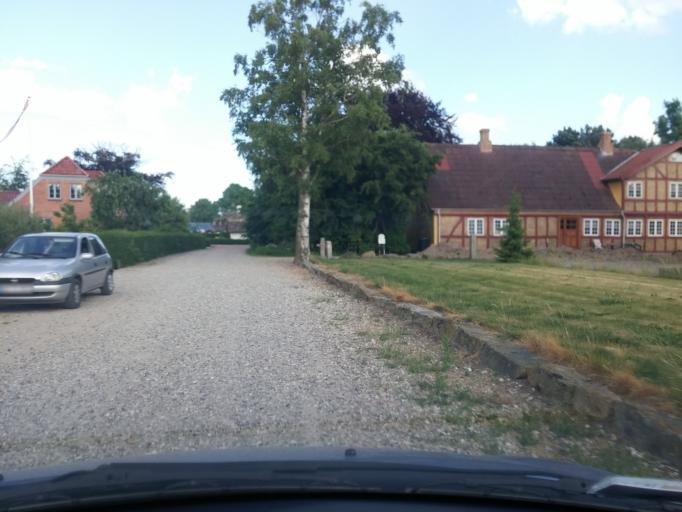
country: DK
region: South Denmark
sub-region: Kerteminde Kommune
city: Langeskov
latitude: 55.3815
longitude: 10.5621
